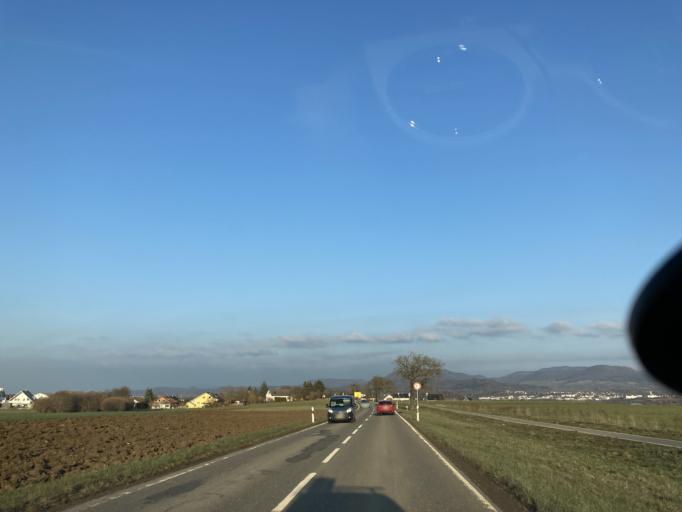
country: DE
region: Baden-Wuerttemberg
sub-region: Tuebingen Region
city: Ofterdingen
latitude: 48.4187
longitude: 9.0123
